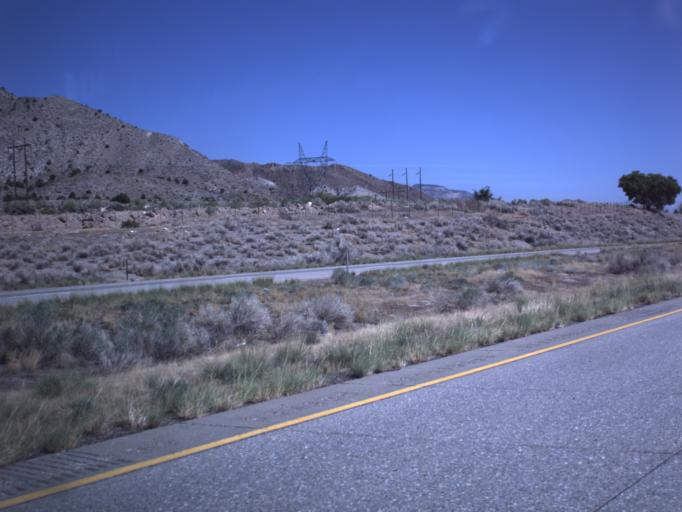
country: US
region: Utah
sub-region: Sevier County
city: Richfield
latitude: 38.7323
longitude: -112.1201
